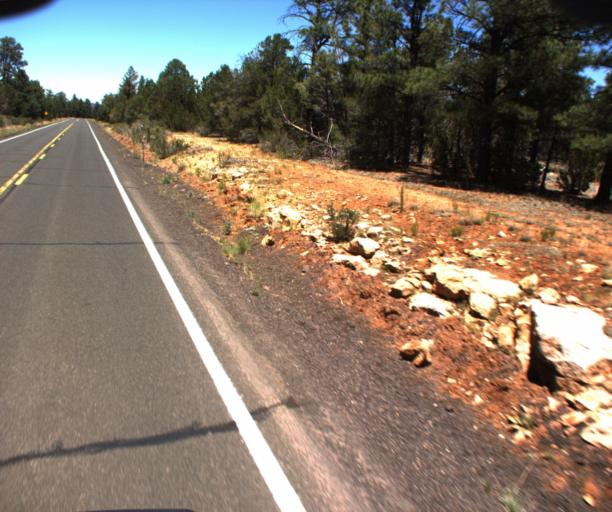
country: US
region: Arizona
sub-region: Gila County
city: Star Valley
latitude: 34.6782
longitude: -111.1122
